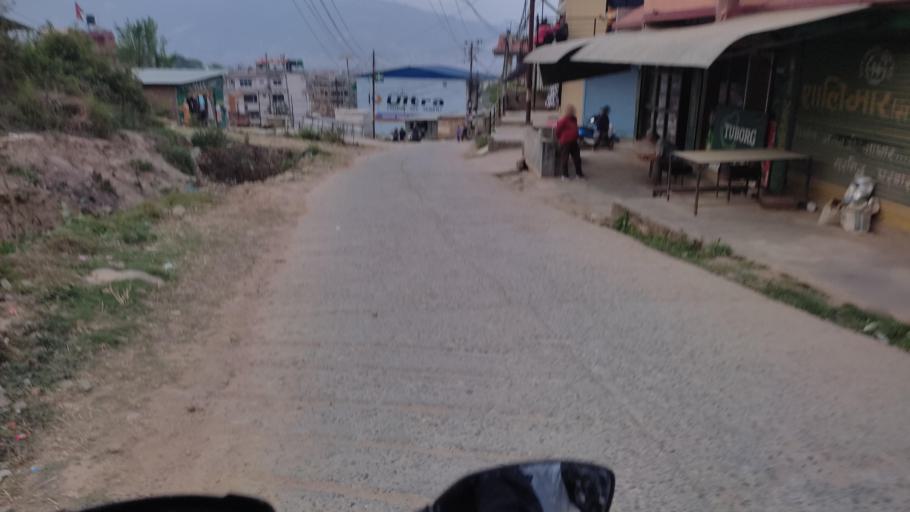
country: NP
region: Central Region
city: Kirtipur
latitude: 27.6728
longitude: 85.2446
